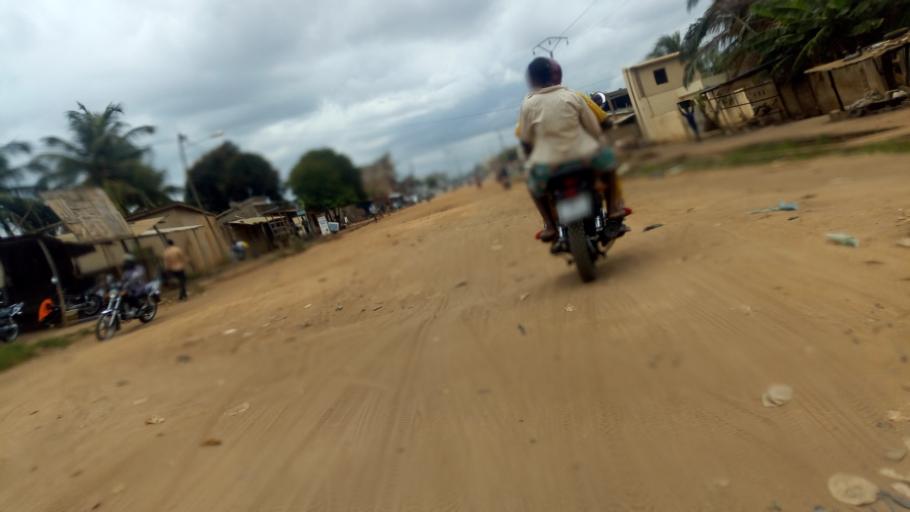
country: TG
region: Maritime
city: Lome
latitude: 6.2251
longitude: 1.1912
